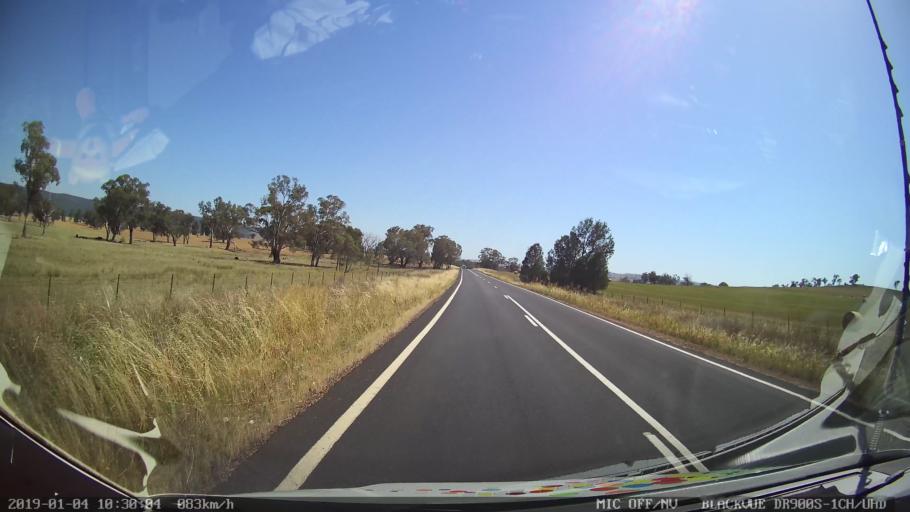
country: AU
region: New South Wales
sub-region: Cabonne
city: Canowindra
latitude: -33.3500
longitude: 148.6257
